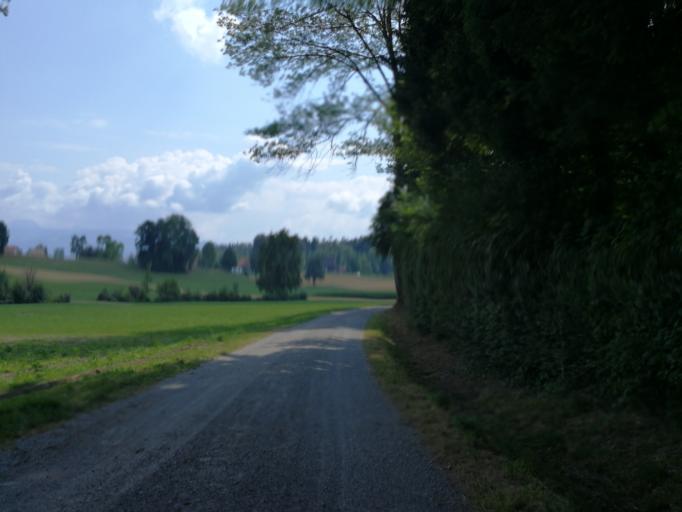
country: CH
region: Zurich
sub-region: Bezirk Hinwil
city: Binzikon
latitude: 47.2696
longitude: 8.7572
